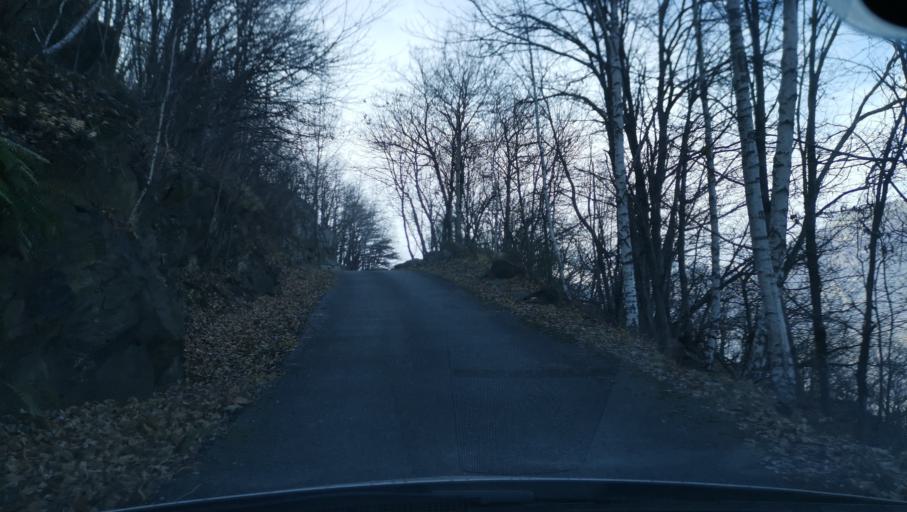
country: IT
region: Piedmont
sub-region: Provincia di Torino
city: Tavagnasco
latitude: 45.5408
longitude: 7.8140
